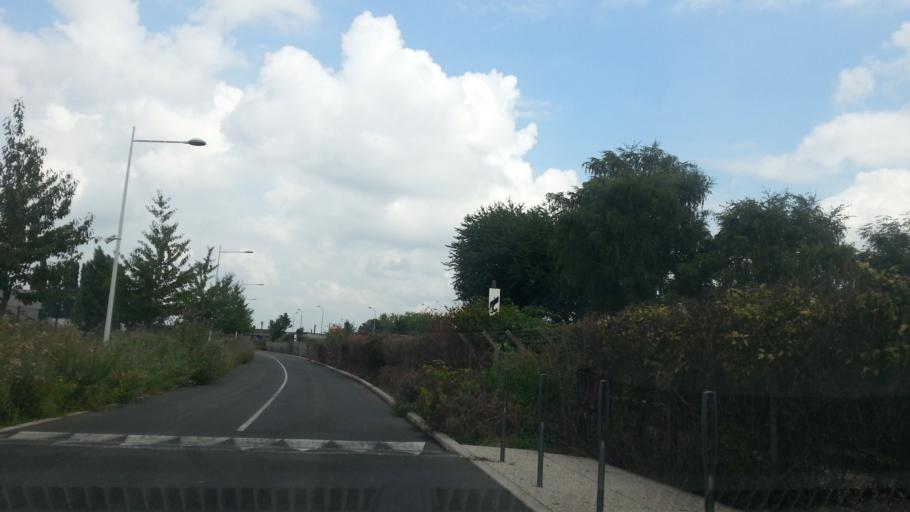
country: FR
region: Picardie
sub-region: Departement de l'Oise
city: Nogent-sur-Oise
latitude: 49.2569
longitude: 2.4590
